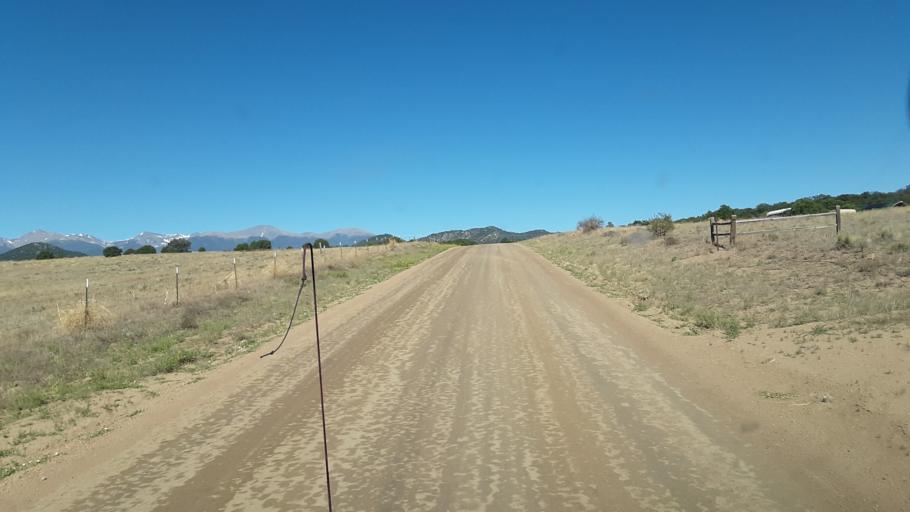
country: US
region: Colorado
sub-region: Custer County
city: Westcliffe
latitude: 38.2845
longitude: -105.4944
